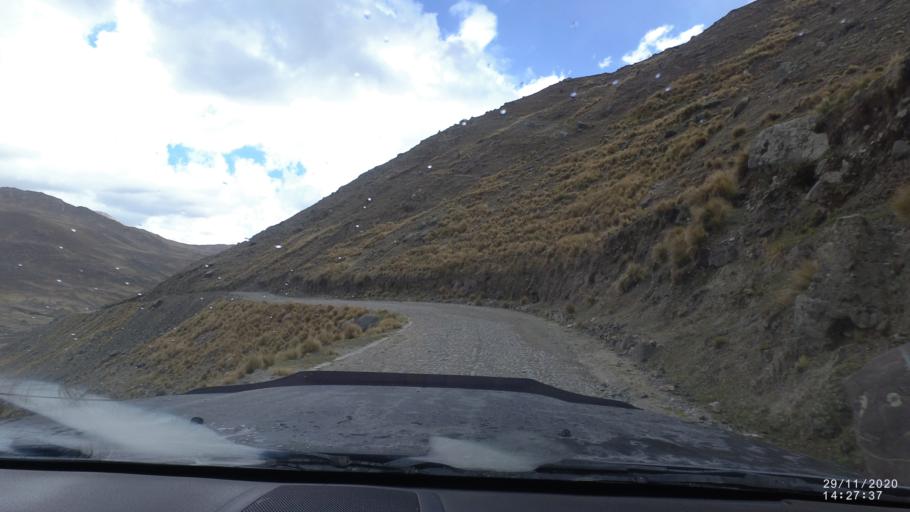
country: BO
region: Cochabamba
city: Sipe Sipe
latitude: -17.2590
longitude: -66.3650
